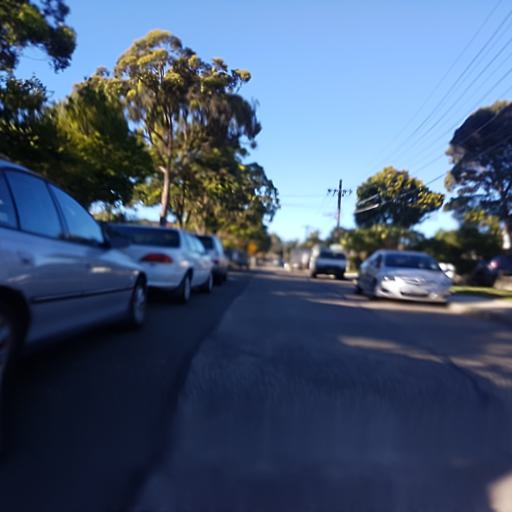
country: AU
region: New South Wales
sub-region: North Sydney
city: St Leonards
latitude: -33.8097
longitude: 151.2024
